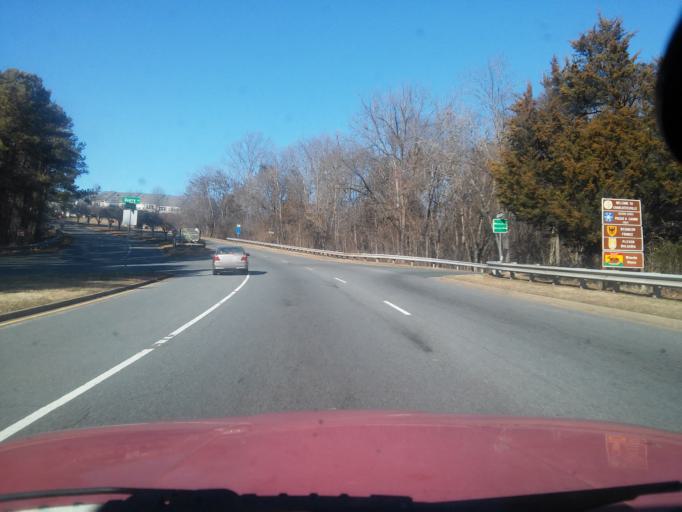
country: US
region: Virginia
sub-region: City of Charlottesville
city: Charlottesville
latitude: 38.0145
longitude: -78.4747
